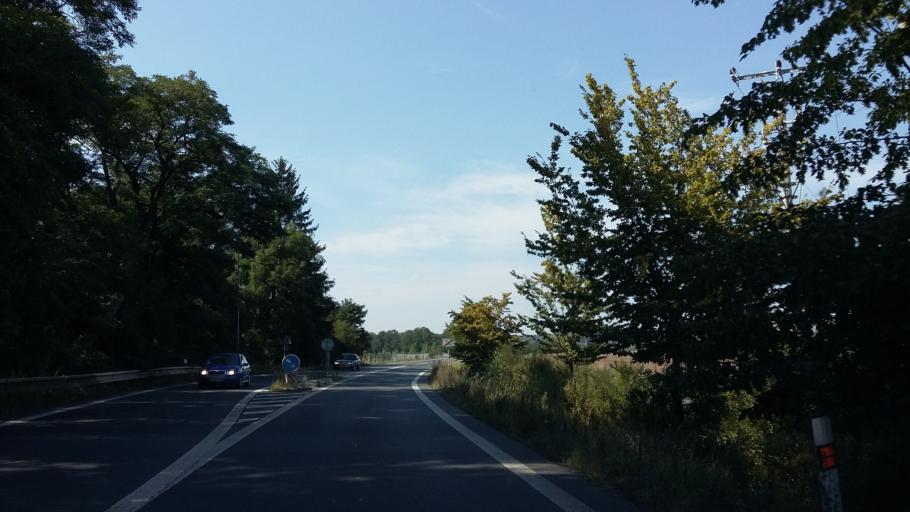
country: CZ
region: Central Bohemia
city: Velky Osek
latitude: 50.1088
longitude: 15.1898
